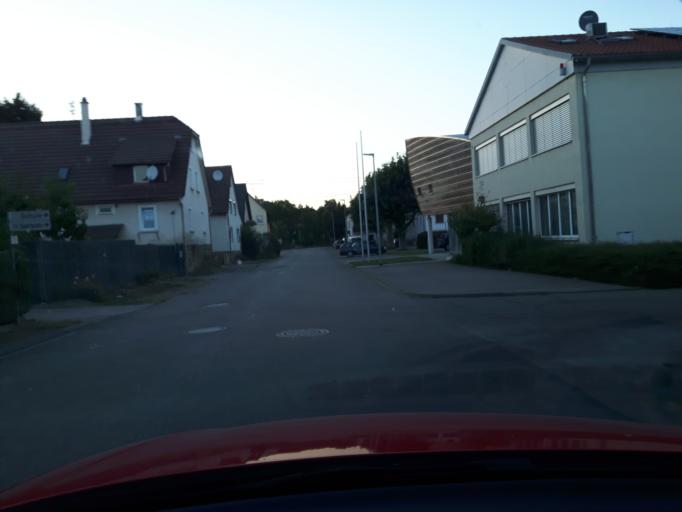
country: DE
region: Baden-Wuerttemberg
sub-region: Regierungsbezirk Stuttgart
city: Pfaffenhofen
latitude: 49.0612
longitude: 8.9759
